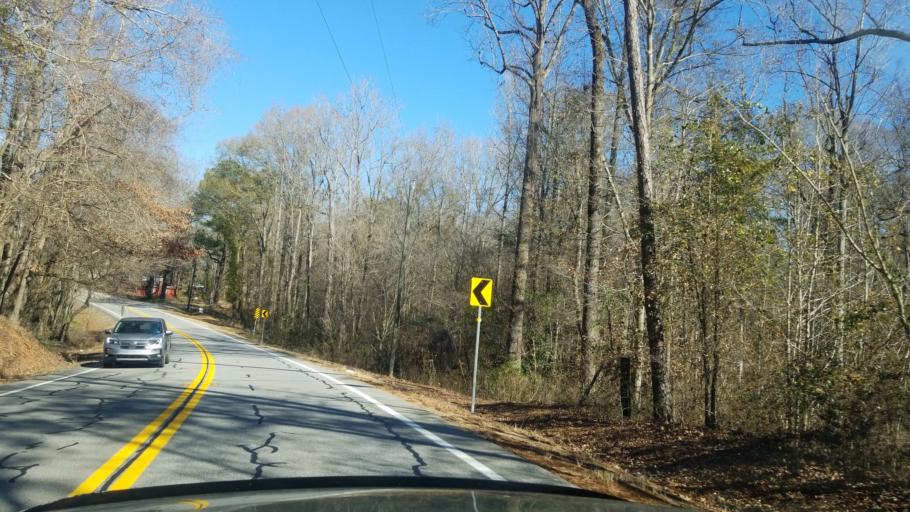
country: US
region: Georgia
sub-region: Harris County
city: Hamilton
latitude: 32.6622
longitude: -84.8591
